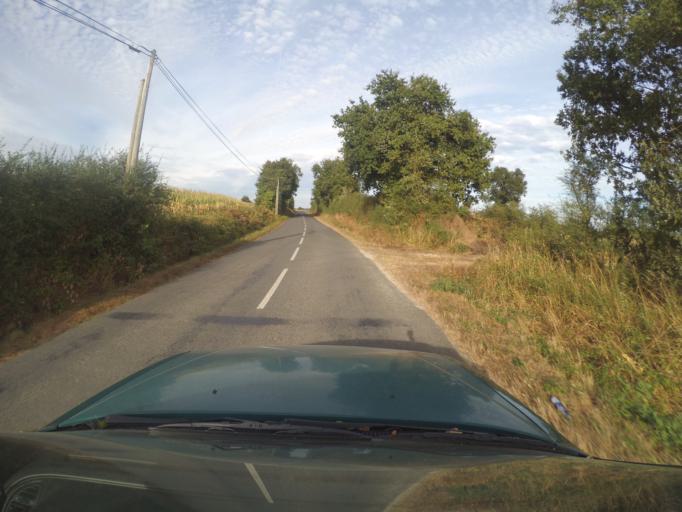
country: FR
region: Pays de la Loire
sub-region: Departement de la Loire-Atlantique
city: Saint-Hilaire-de-Clisson
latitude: 47.0610
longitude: -1.3290
